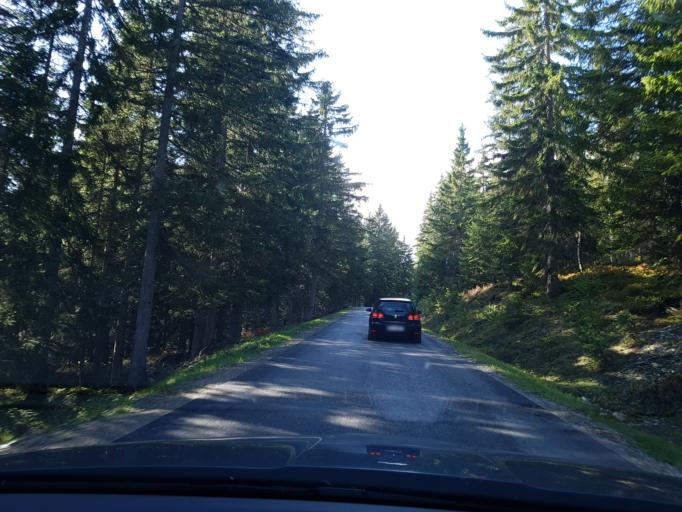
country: AT
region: Salzburg
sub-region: Politischer Bezirk Sankt Johann im Pongau
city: Filzmoos
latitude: 47.4091
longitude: 13.5105
